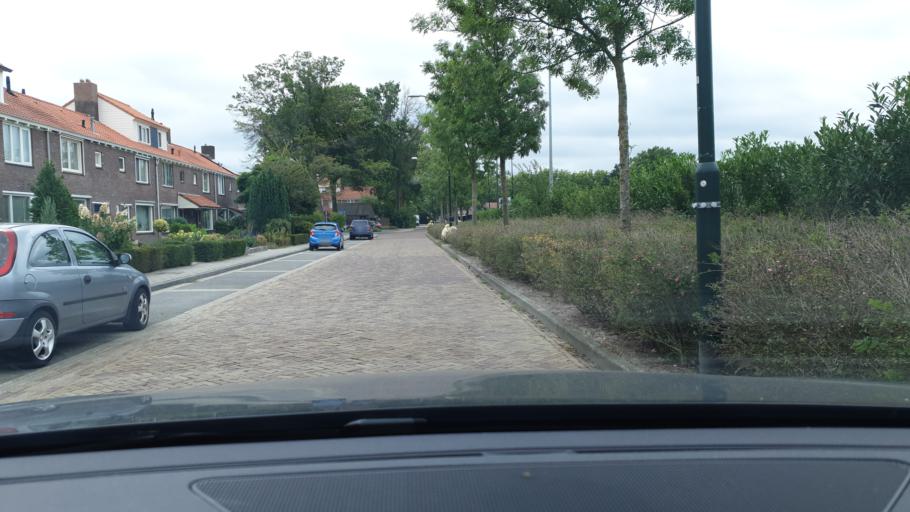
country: NL
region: North Brabant
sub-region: Gemeente Waalre
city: Waalre
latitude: 51.3994
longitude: 5.4835
